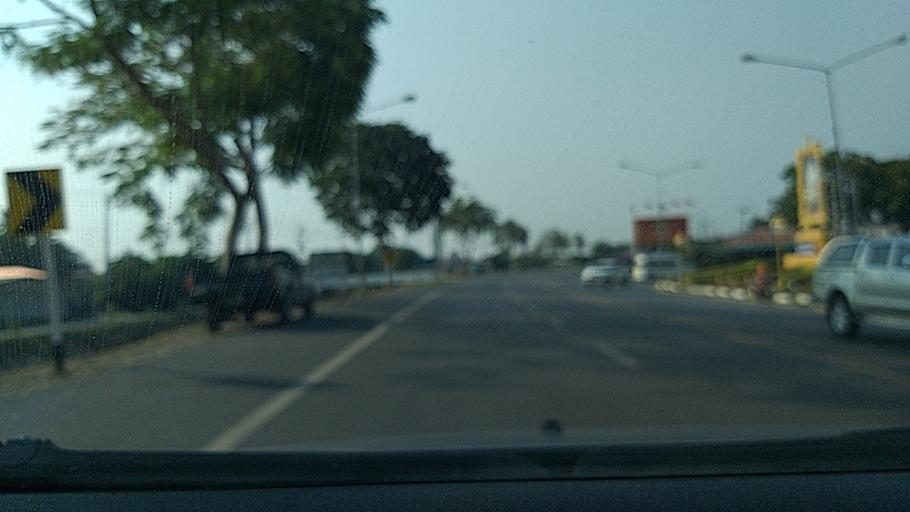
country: TH
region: Ang Thong
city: Chaiyo
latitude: 14.7153
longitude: 100.4350
